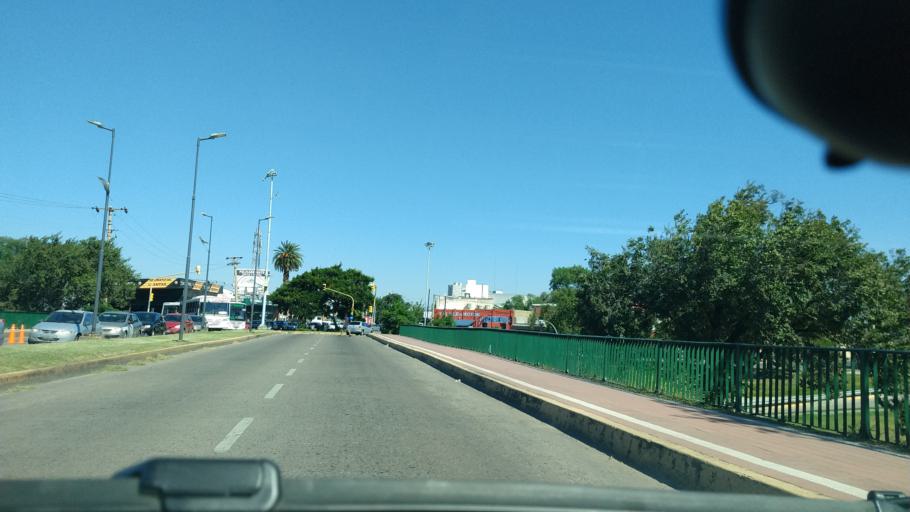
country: AR
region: Cordoba
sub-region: Departamento de Capital
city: Cordoba
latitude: -31.3919
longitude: -64.2126
